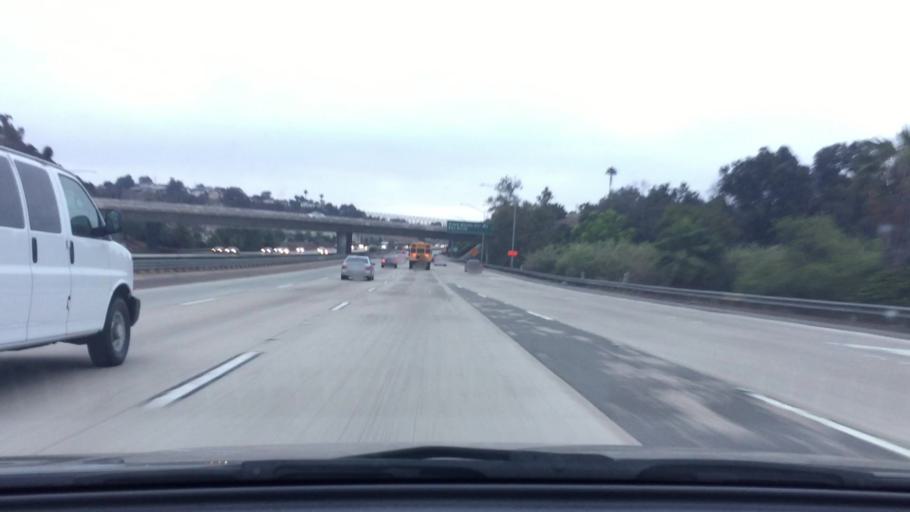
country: US
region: California
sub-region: San Diego County
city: Chula Vista
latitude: 32.6594
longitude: -117.0702
